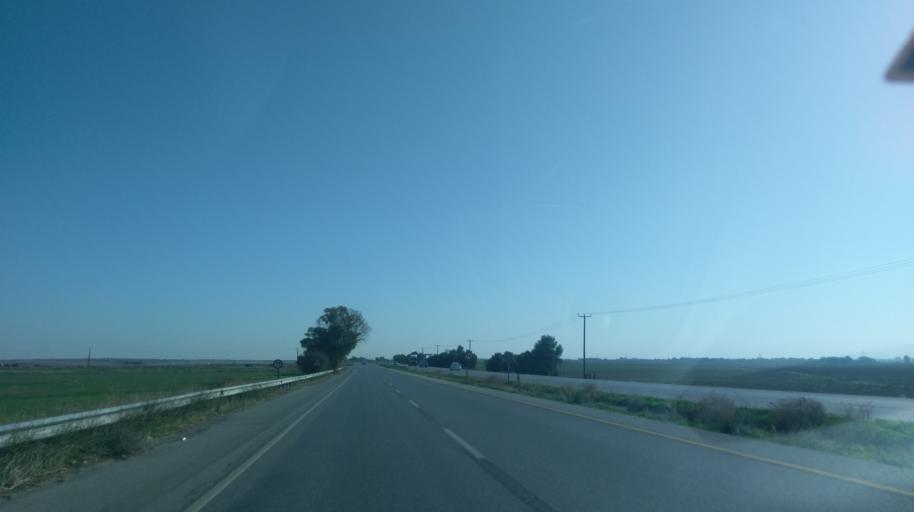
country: CY
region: Larnaka
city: Athienou
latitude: 35.2111
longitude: 33.5546
